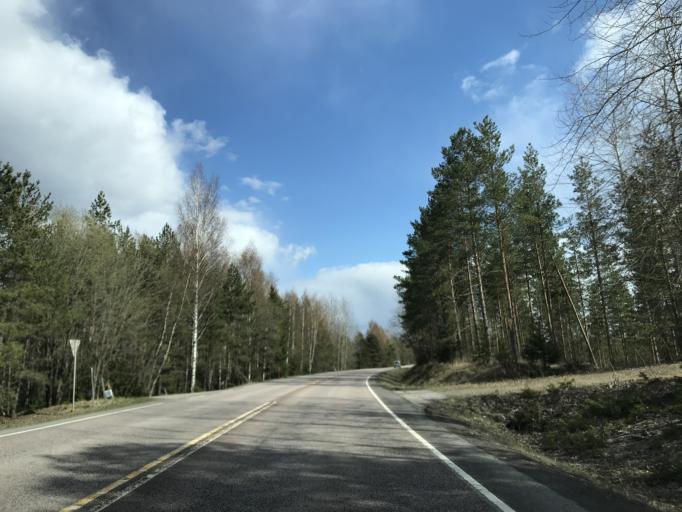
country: FI
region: Uusimaa
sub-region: Helsinki
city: Hyvinge
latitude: 60.5418
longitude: 24.8826
